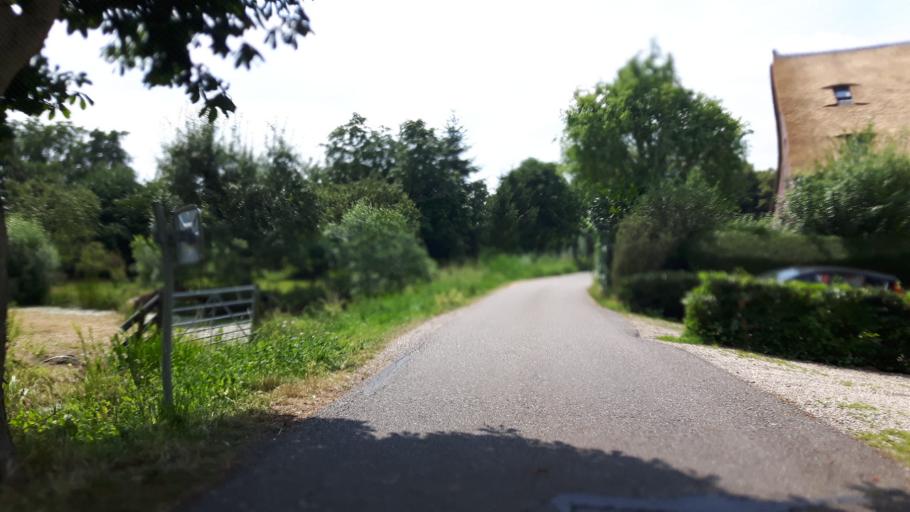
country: NL
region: South Holland
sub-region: Gemeente Giessenlanden
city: Giessenburg
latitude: 51.9103
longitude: 4.9123
